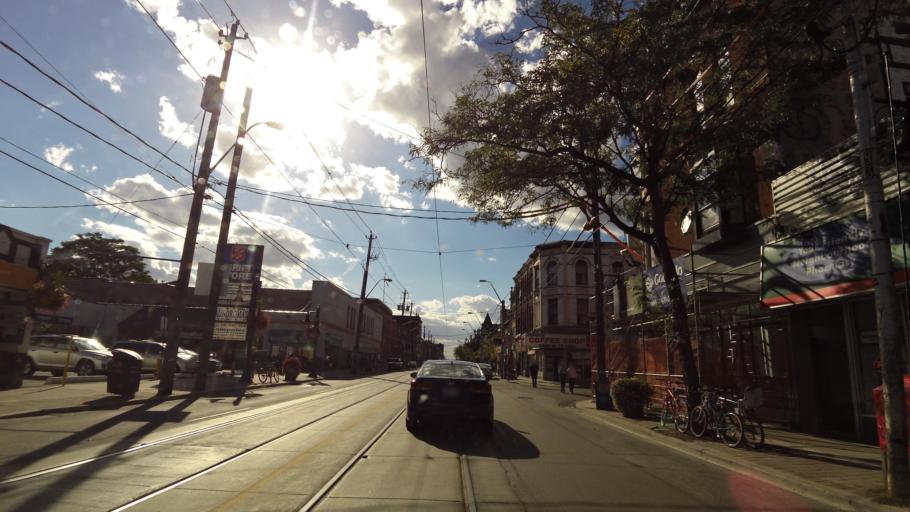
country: CA
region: Ontario
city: Toronto
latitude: 43.6404
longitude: -79.4374
